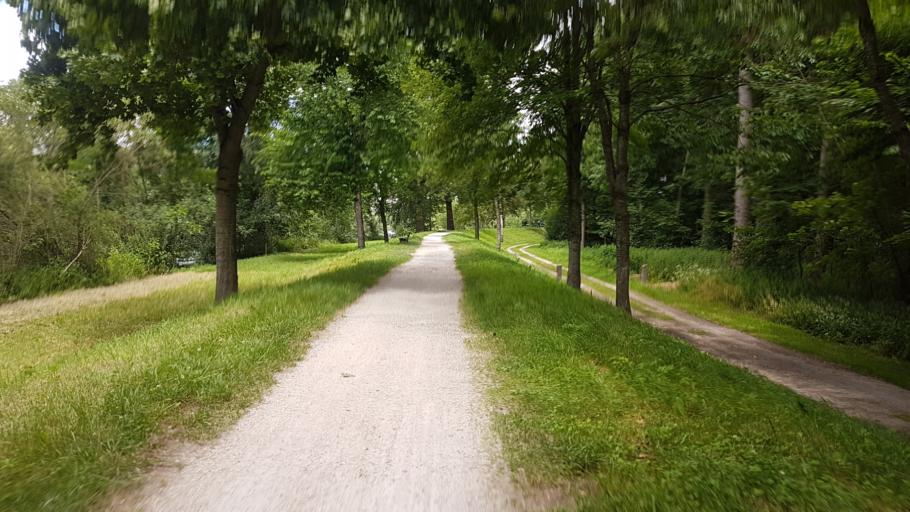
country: DE
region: Baden-Wuerttemberg
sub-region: Tuebingen Region
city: Neufra
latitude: 48.1372
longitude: 9.4662
